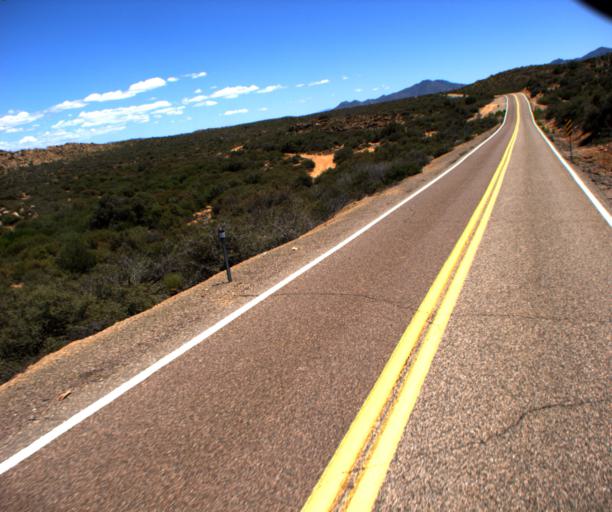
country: US
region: Arizona
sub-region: Yavapai County
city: Bagdad
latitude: 34.4441
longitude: -112.9385
